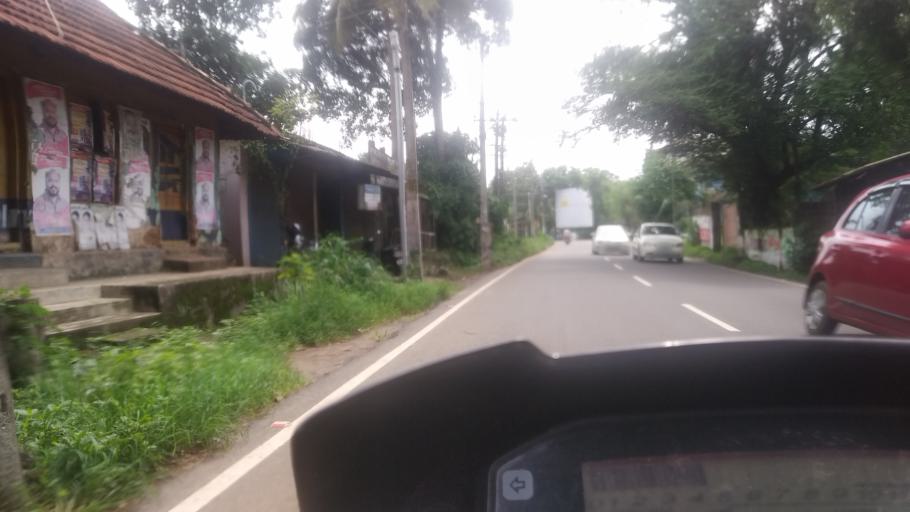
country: IN
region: Kerala
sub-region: Ernakulam
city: Aluva
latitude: 10.1296
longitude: 76.2983
